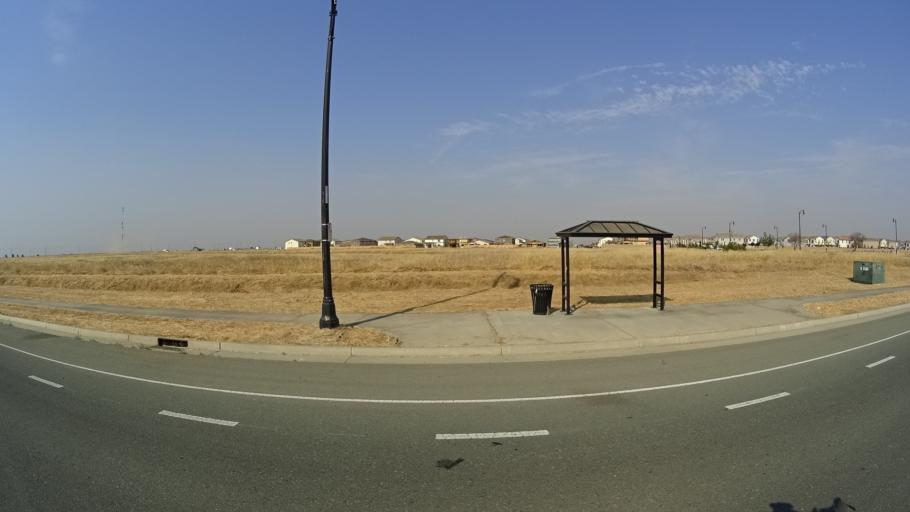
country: US
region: California
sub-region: Sacramento County
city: Elk Grove
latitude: 38.3785
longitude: -121.3721
